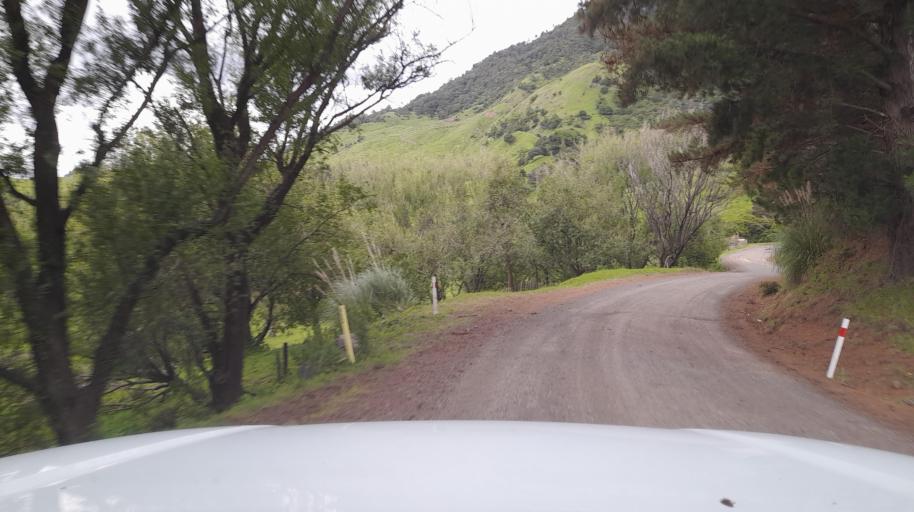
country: NZ
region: Northland
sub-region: Far North District
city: Kaitaia
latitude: -35.3382
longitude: 173.3580
